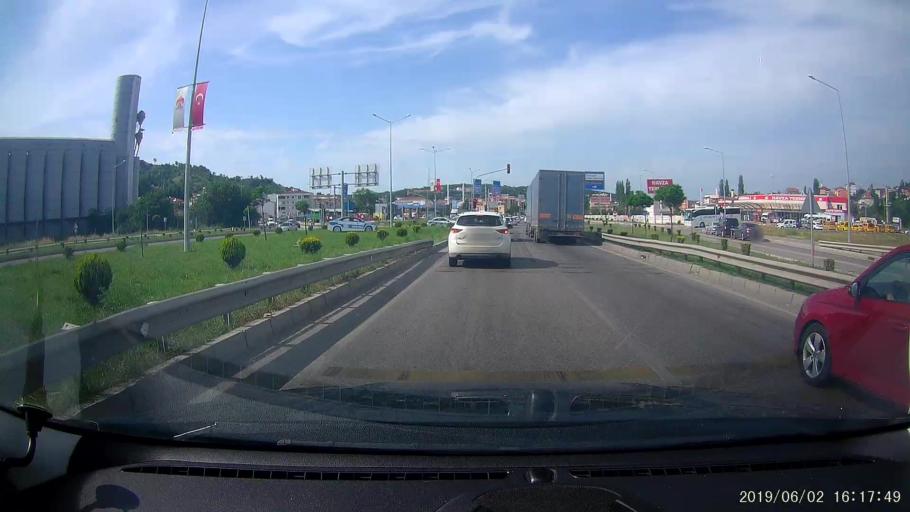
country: TR
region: Samsun
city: Havza
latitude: 40.9608
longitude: 35.6662
